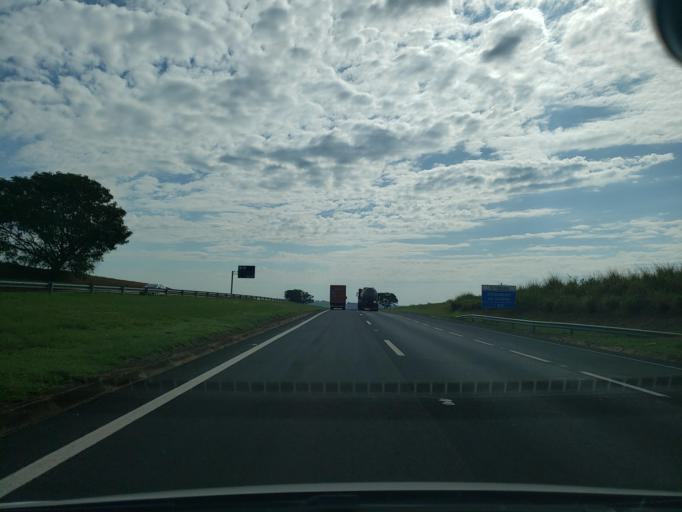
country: BR
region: Sao Paulo
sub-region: Lins
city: Lins
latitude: -21.6643
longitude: -49.7915
